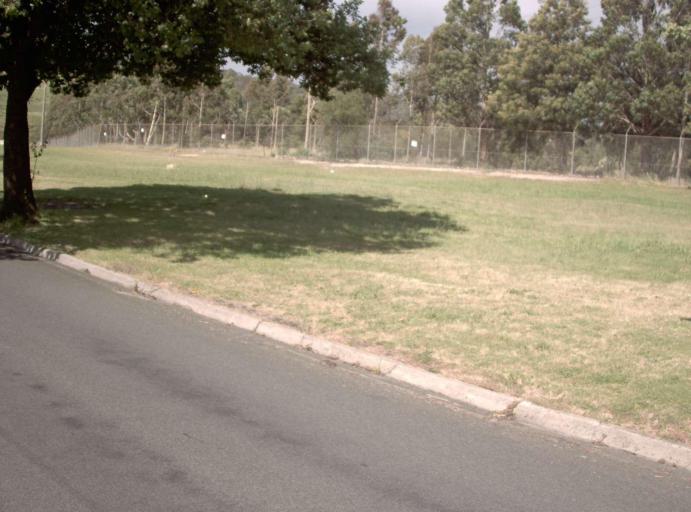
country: AU
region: Victoria
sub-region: Latrobe
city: Morwell
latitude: -38.1622
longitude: 146.3674
